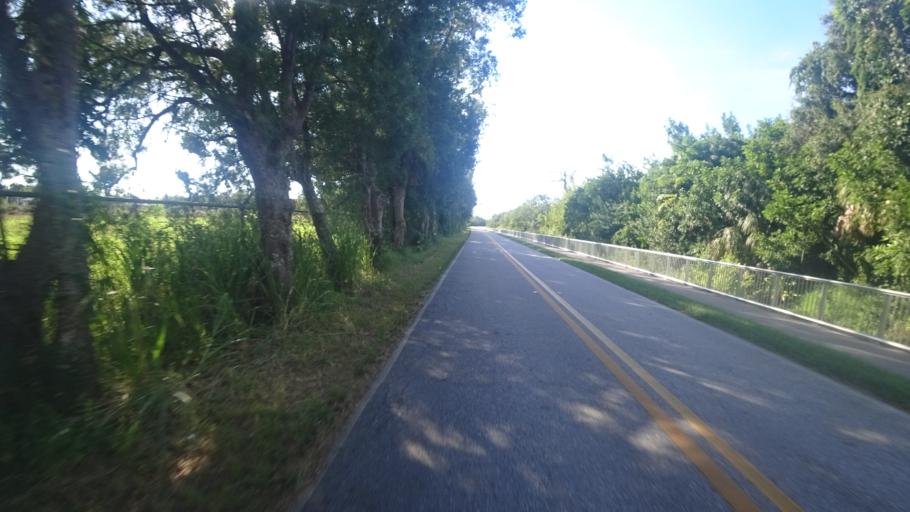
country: US
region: Florida
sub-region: Manatee County
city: West Bradenton
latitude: 27.5298
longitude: -82.6174
